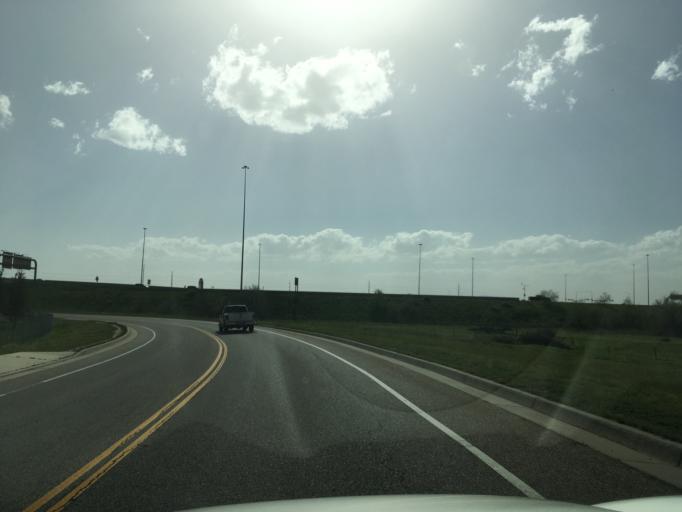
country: US
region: Utah
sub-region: Davis County
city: Farmington
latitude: 40.9900
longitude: -111.8993
